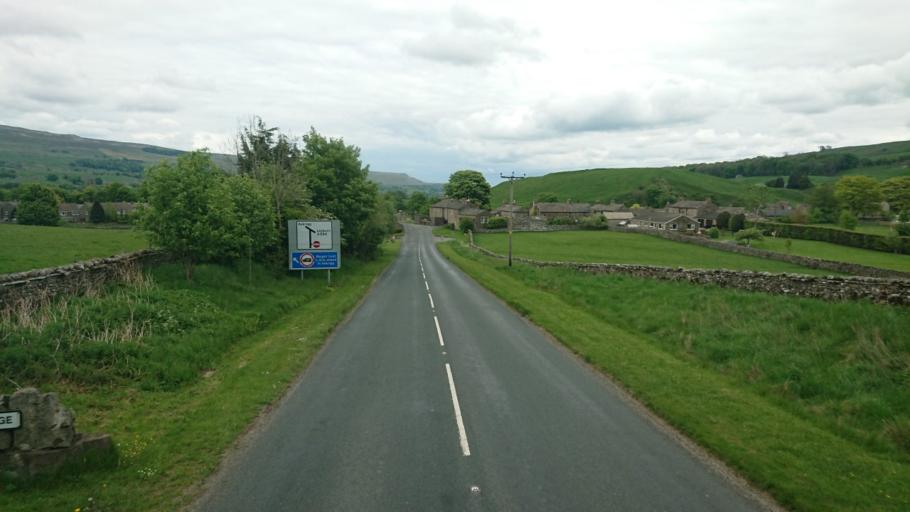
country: GB
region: England
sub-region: County Durham
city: Bowes
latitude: 54.3084
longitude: -2.1065
